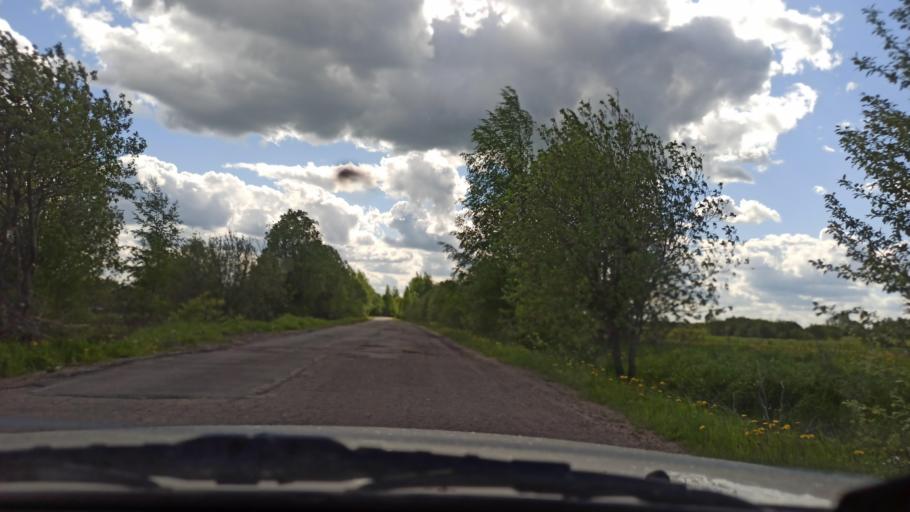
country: RU
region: Vologda
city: Molochnoye
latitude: 59.3742
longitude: 39.7074
